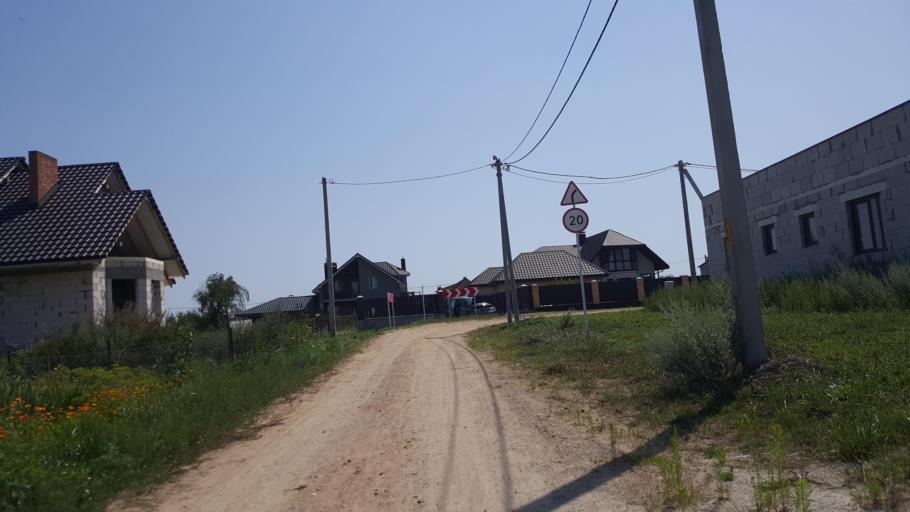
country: BY
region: Brest
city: Zhabinka
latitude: 52.1988
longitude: 23.9901
